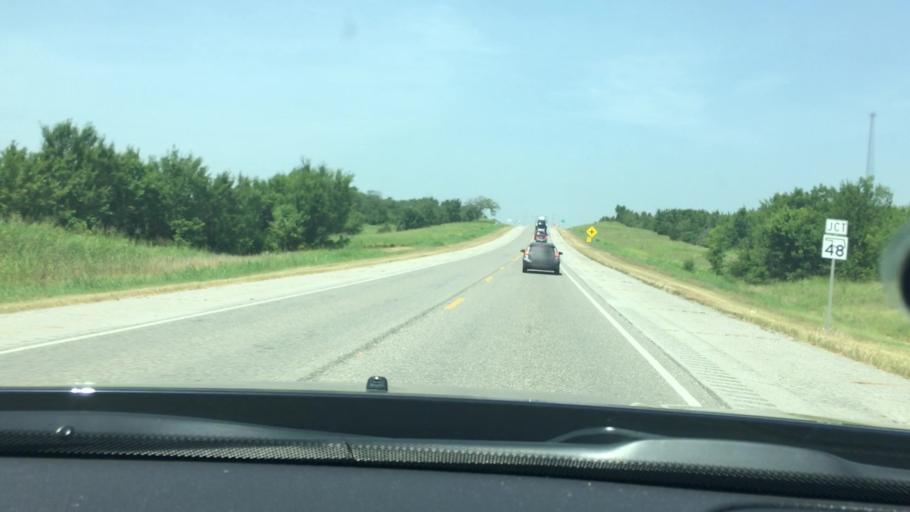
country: US
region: Oklahoma
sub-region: Coal County
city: Coalgate
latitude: 34.6110
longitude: -96.4183
